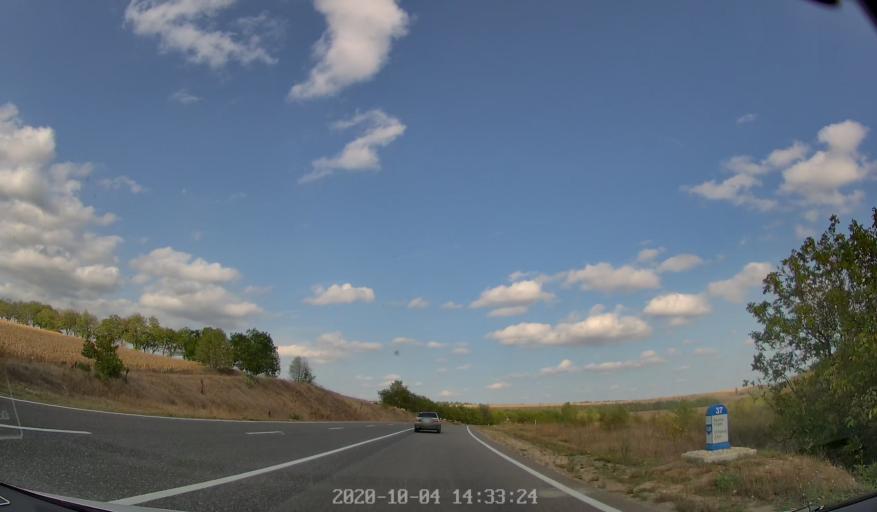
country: MD
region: Soldanesti
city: Soldanesti
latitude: 47.6973
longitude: 28.8285
